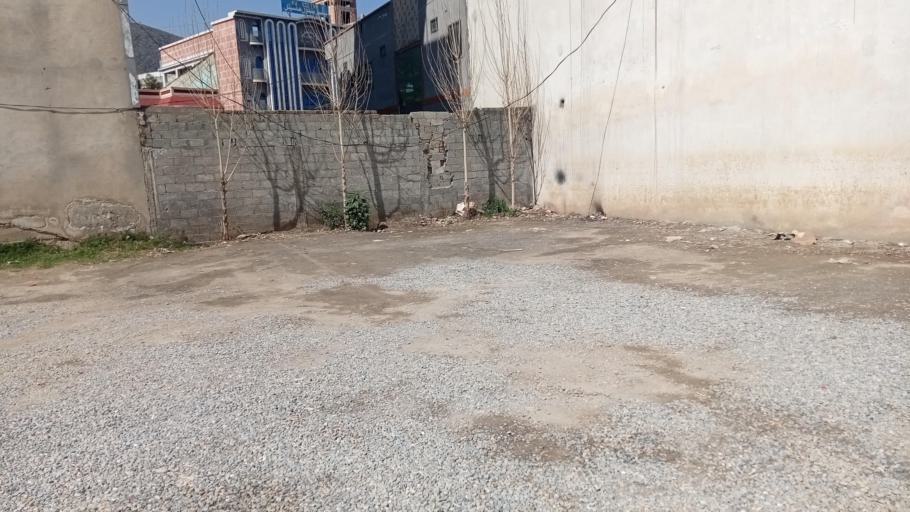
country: PK
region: Khyber Pakhtunkhwa
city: Saidu Sharif
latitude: 34.7602
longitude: 72.3583
